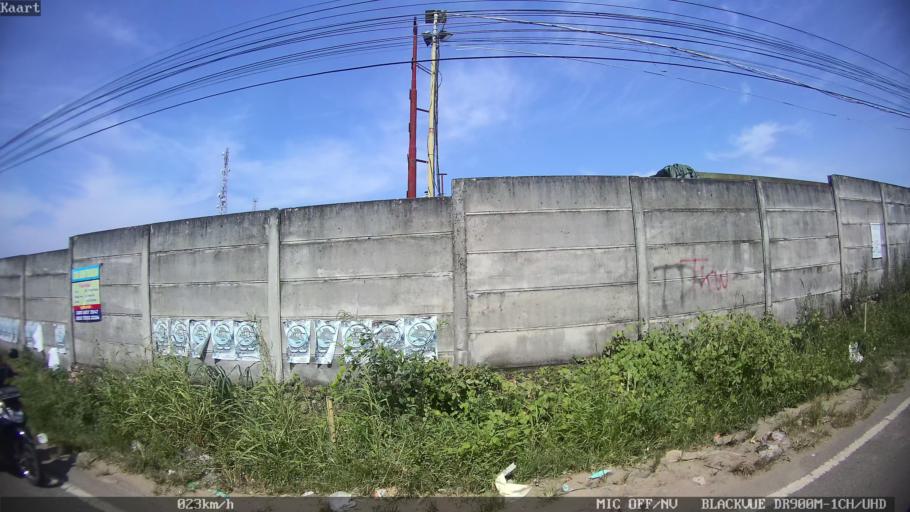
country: ID
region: Lampung
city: Kedaton
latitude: -5.3654
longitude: 105.2569
